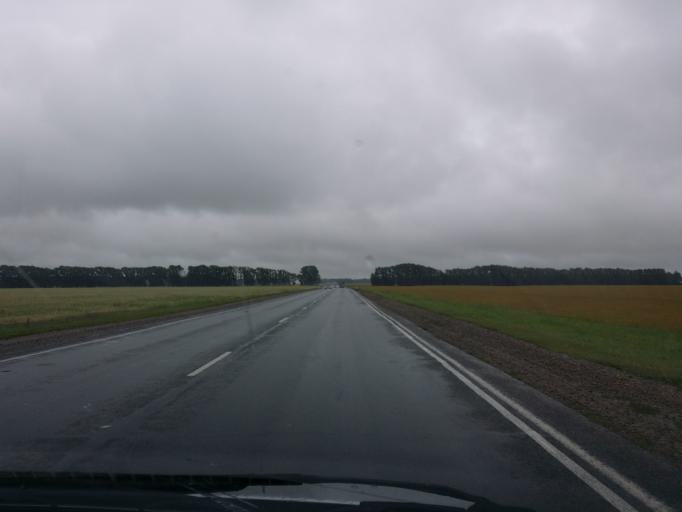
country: RU
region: Altai Krai
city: Bayunovskiye Klyuchi
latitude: 53.2815
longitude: 84.3450
